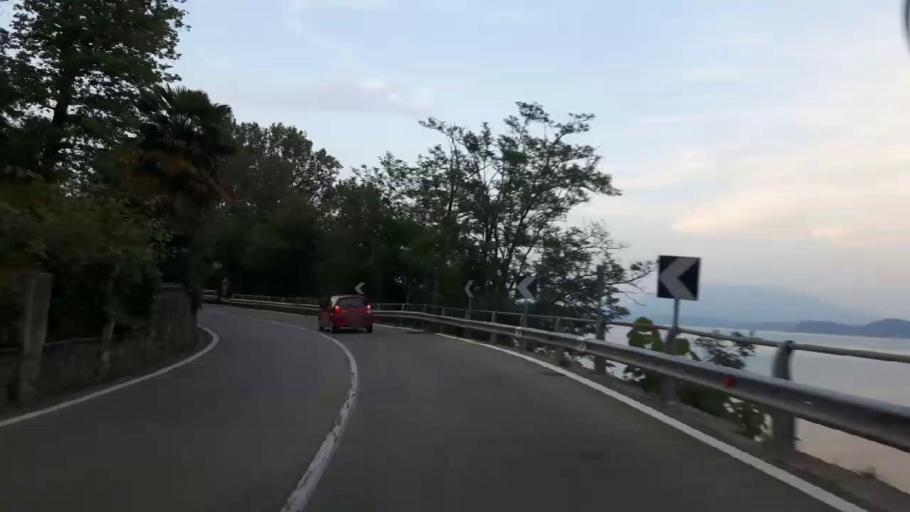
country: IT
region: Piedmont
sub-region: Provincia di Novara
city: Meina
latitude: 45.8073
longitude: 8.5428
